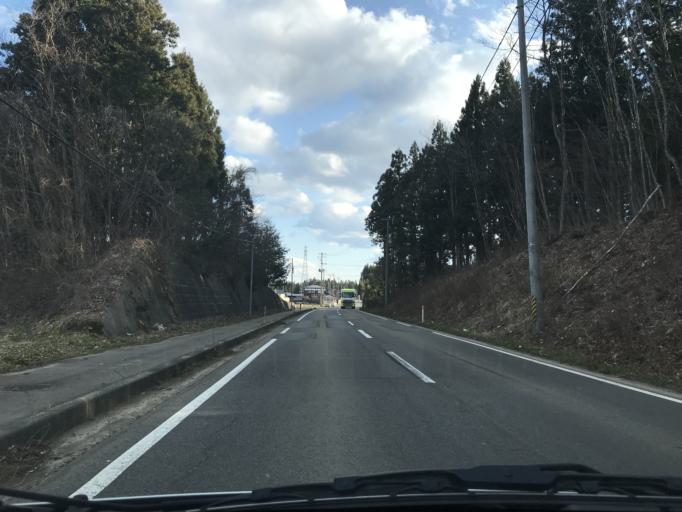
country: JP
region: Iwate
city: Kitakami
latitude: 39.3304
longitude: 141.0391
